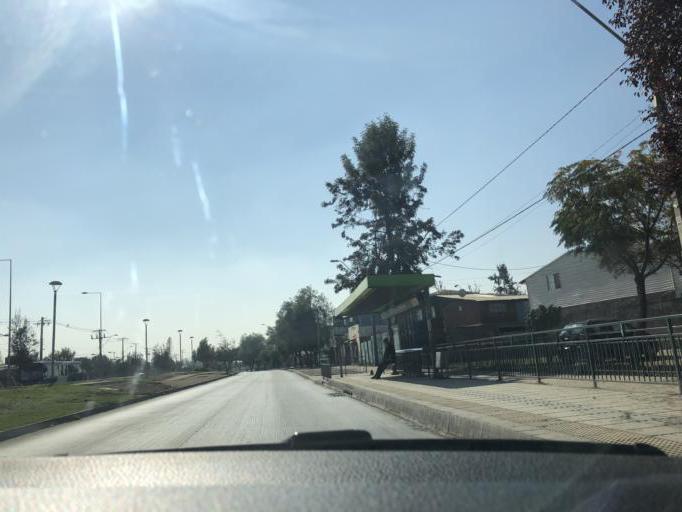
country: CL
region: Santiago Metropolitan
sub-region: Provincia de Santiago
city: La Pintana
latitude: -33.6277
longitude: -70.6285
